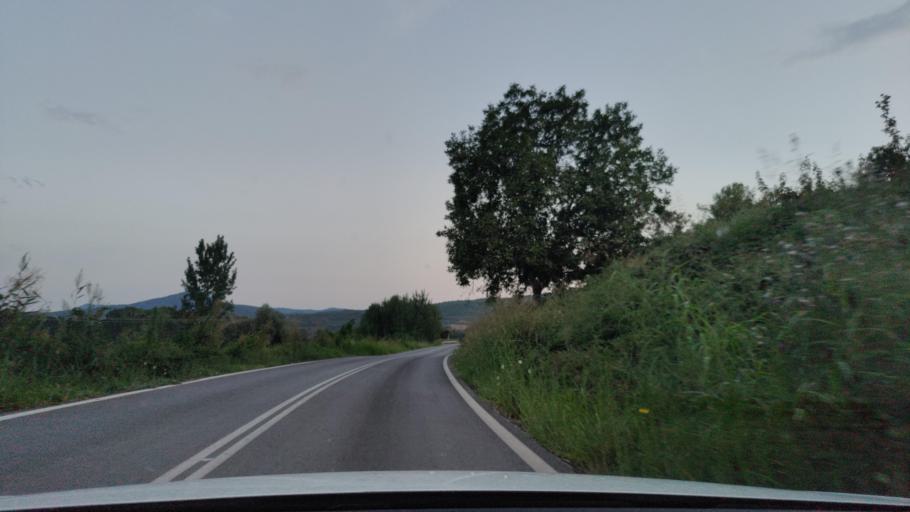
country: GR
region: Central Macedonia
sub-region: Nomos Serron
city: Chrysochorafa
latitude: 41.1410
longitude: 23.2284
